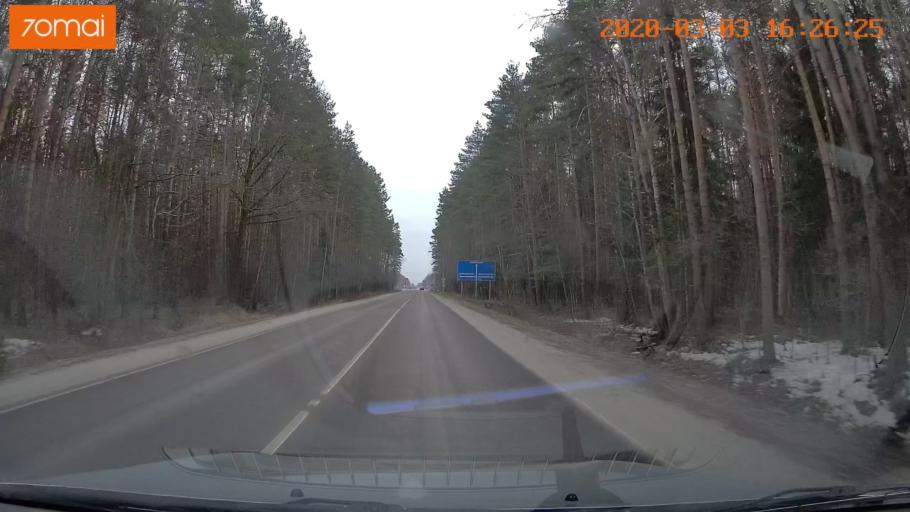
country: RU
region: Moskovskaya
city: Konobeyevo
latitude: 55.4388
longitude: 38.6607
